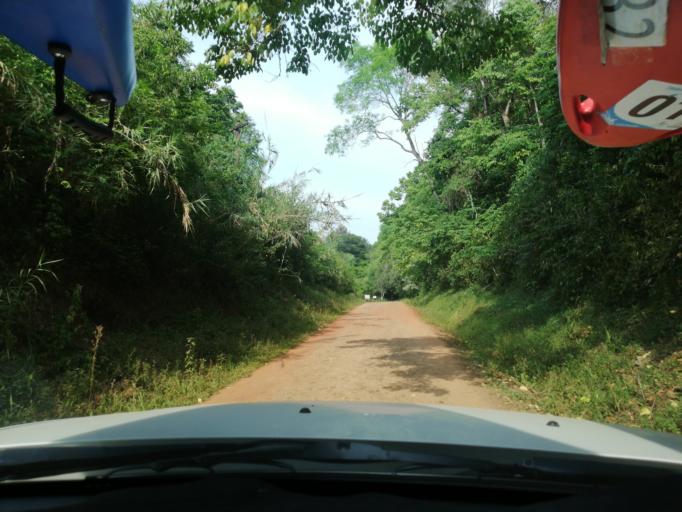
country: AR
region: Misiones
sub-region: Departamento de San Ignacio
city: San Ignacio
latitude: -27.3018
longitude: -55.5784
